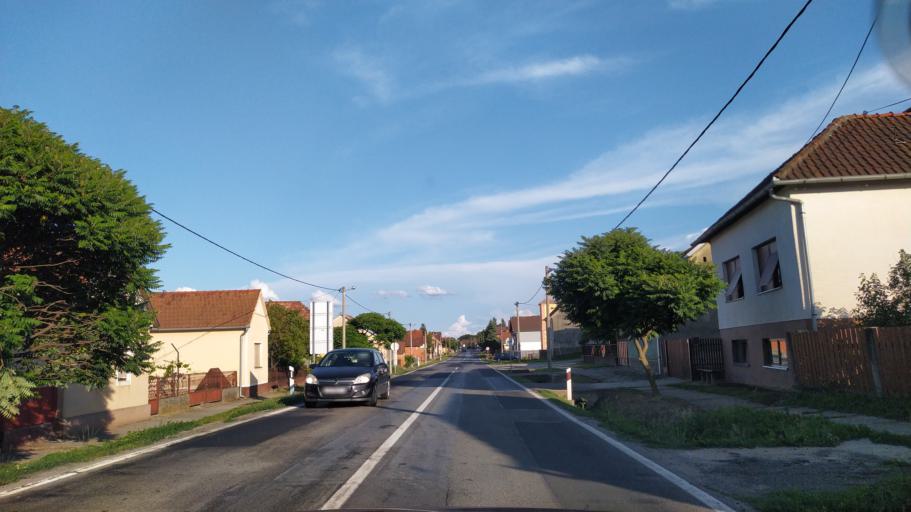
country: HR
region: Virovitick-Podravska
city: Slatina
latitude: 45.6858
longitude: 17.7367
